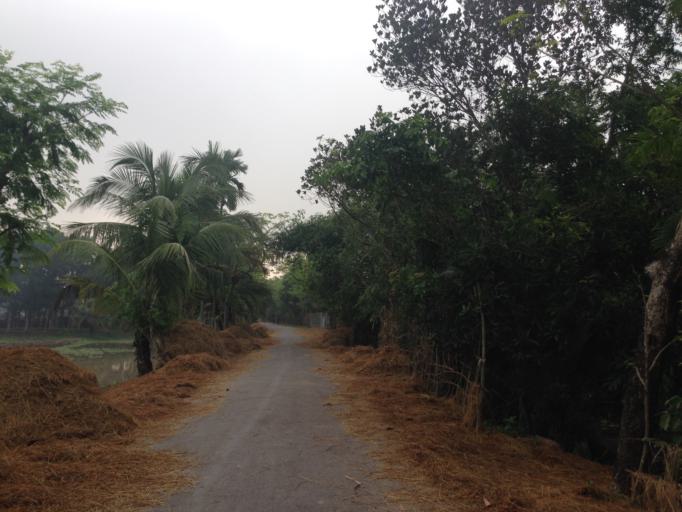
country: BD
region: Khulna
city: Kalia
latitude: 23.0405
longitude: 89.6425
